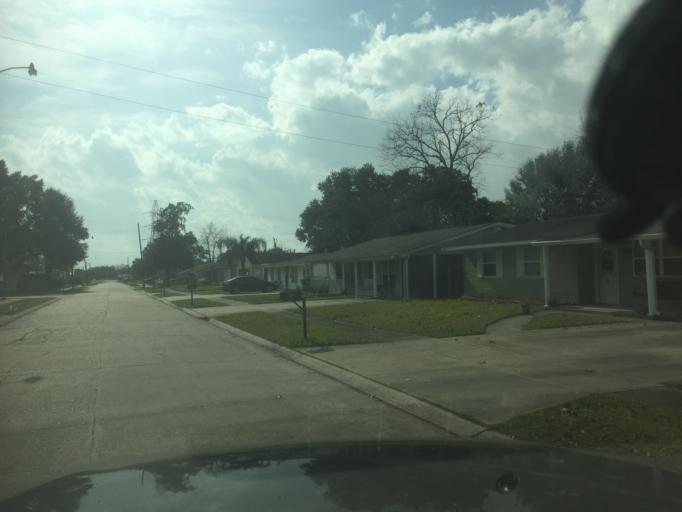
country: US
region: Louisiana
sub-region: Jefferson Parish
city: Avondale
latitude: 29.9133
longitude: -90.2059
